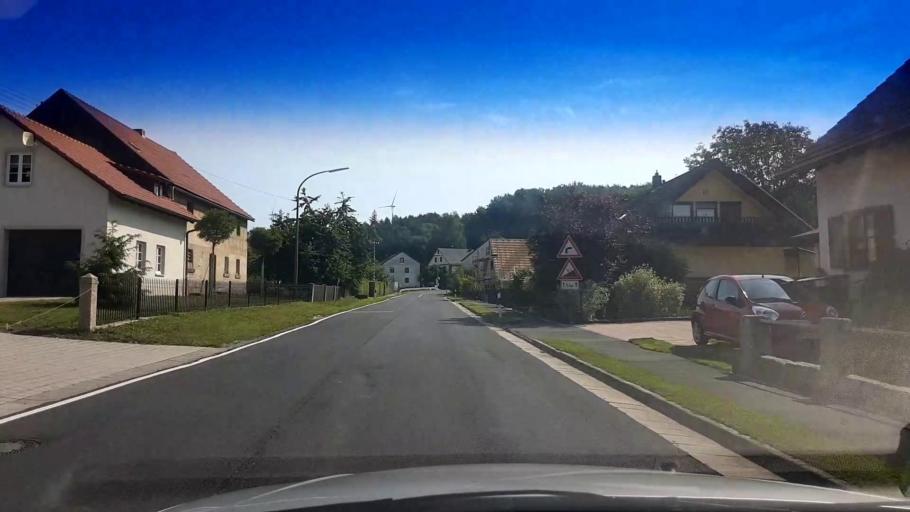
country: DE
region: Bavaria
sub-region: Upper Franconia
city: Mistelgau
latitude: 49.9404
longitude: 11.4002
